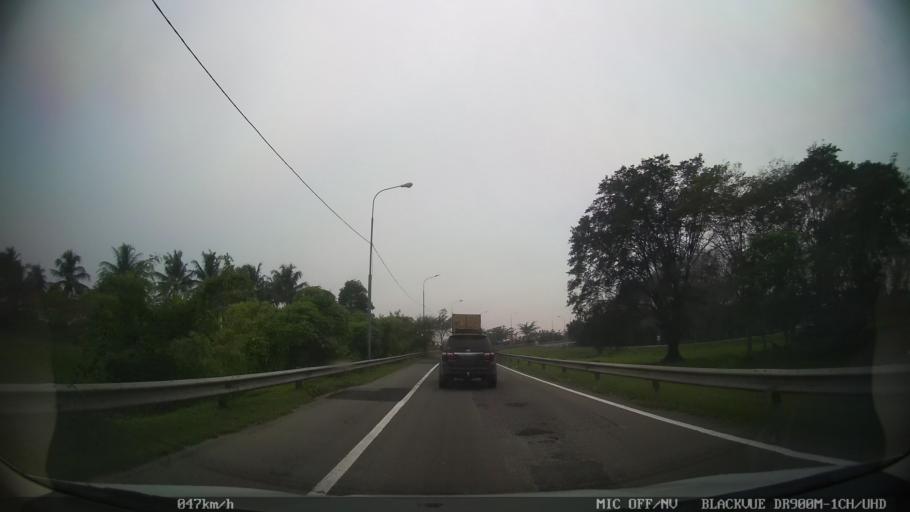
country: ID
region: North Sumatra
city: Deli Tua
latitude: 3.5466
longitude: 98.7256
